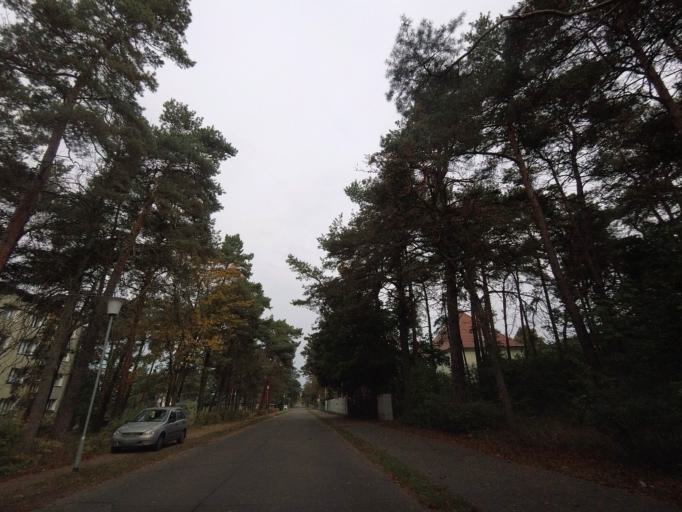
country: DE
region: Brandenburg
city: Niedergorsdorf
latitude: 52.0086
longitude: 12.9939
